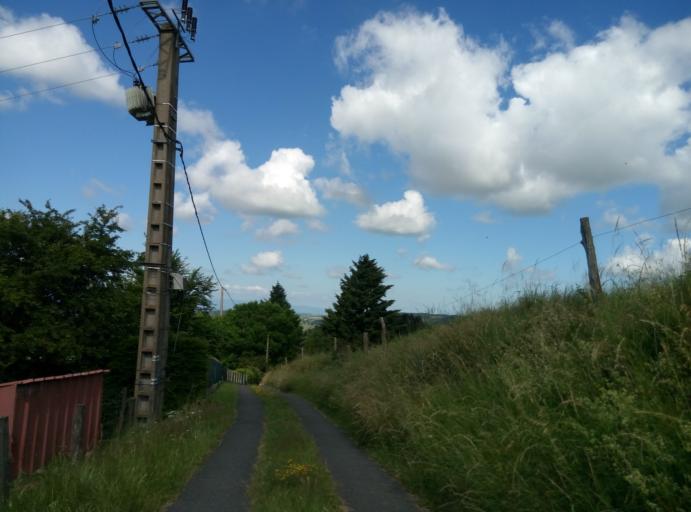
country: FR
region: Rhone-Alpes
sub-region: Departement du Rhone
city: Cublize
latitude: 45.9917
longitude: 4.3955
